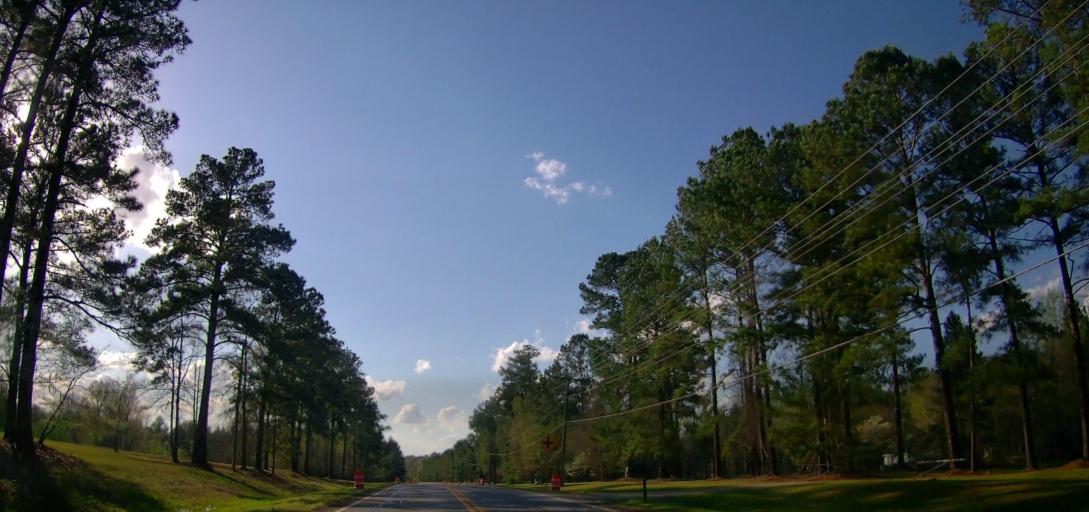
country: US
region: Georgia
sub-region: Putnam County
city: Eatonton
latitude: 33.1701
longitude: -83.3888
